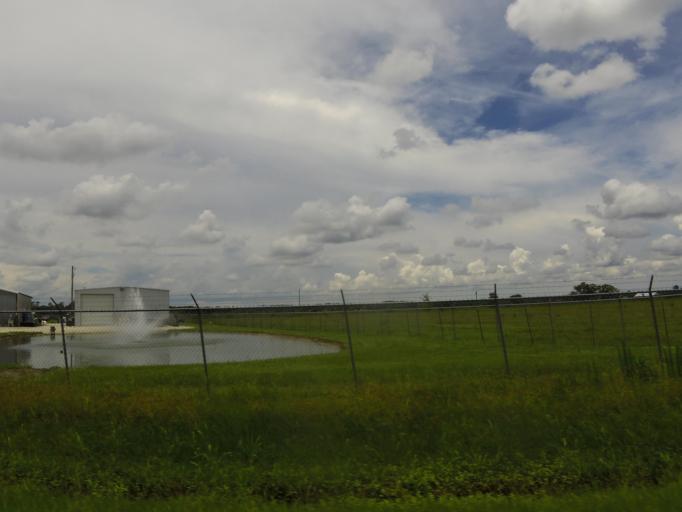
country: US
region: Florida
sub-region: Putnam County
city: East Palatka
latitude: 29.6949
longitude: -81.4888
